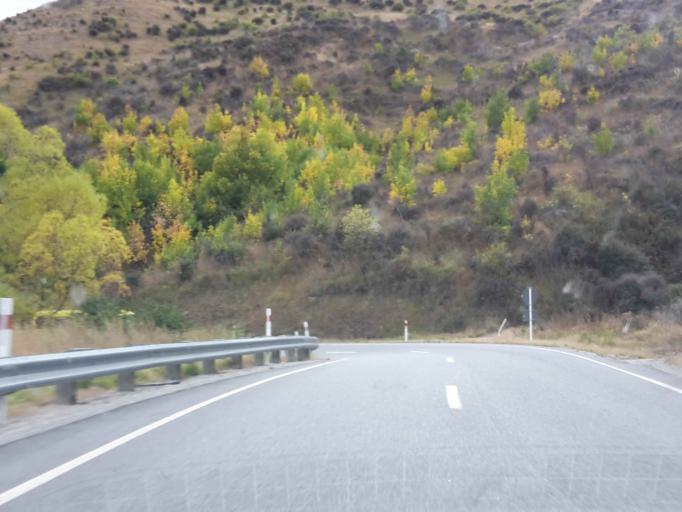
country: NZ
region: Otago
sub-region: Queenstown-Lakes District
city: Arrowtown
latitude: -44.9884
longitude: 168.9046
